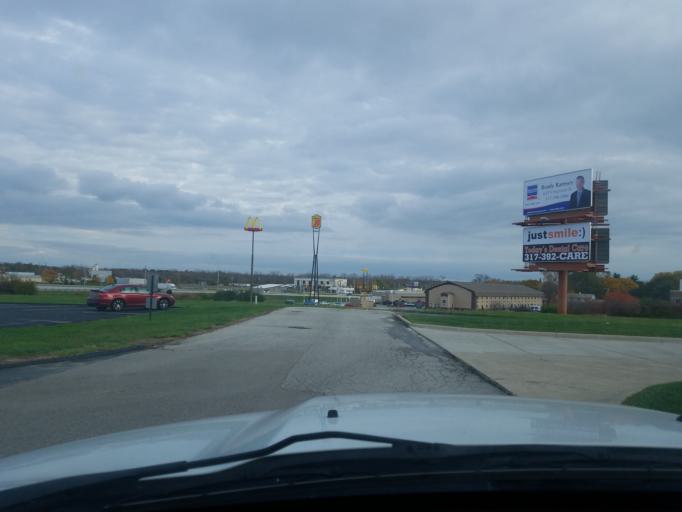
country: US
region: Indiana
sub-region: Shelby County
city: Shelbyville
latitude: 39.5498
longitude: -85.7775
